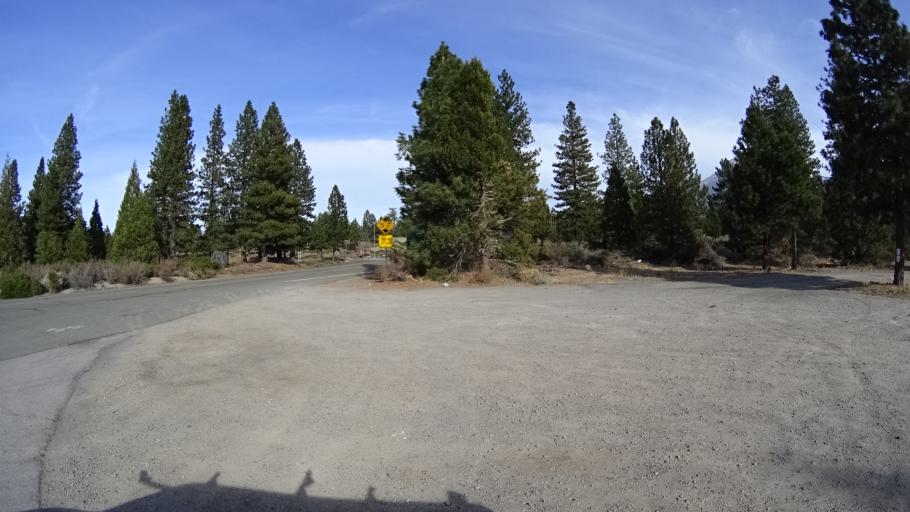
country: US
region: California
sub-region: Siskiyou County
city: Weed
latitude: 41.3950
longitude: -122.3817
